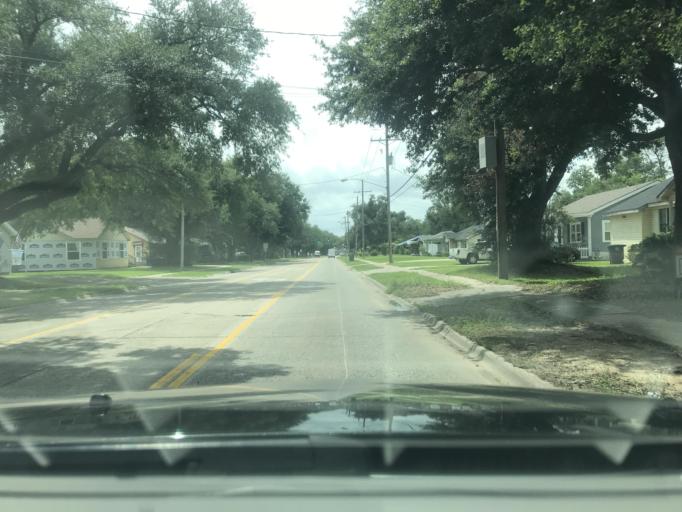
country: US
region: Louisiana
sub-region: Calcasieu Parish
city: Lake Charles
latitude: 30.2130
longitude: -93.1970
